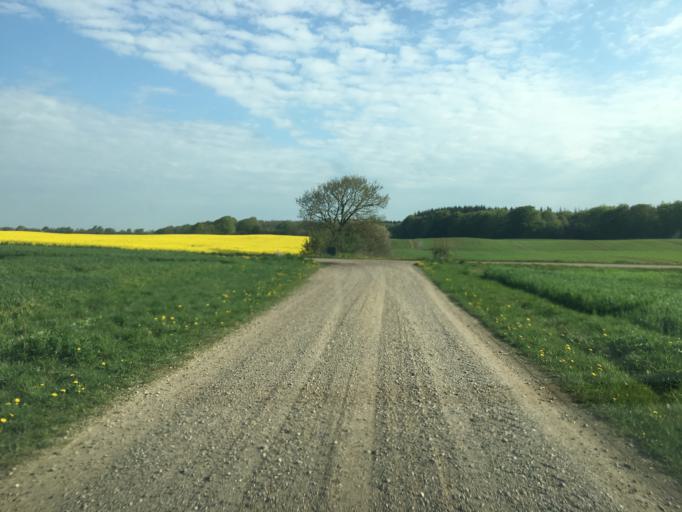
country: DK
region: South Denmark
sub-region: Aabenraa Kommune
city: Lojt Kirkeby
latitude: 55.1586
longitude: 9.3896
